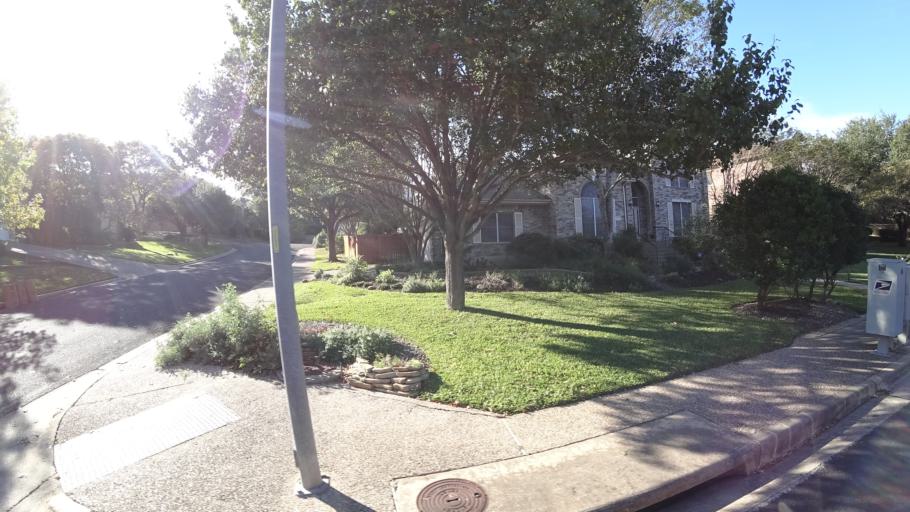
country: US
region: Texas
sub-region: Williamson County
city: Jollyville
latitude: 30.4155
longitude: -97.7755
